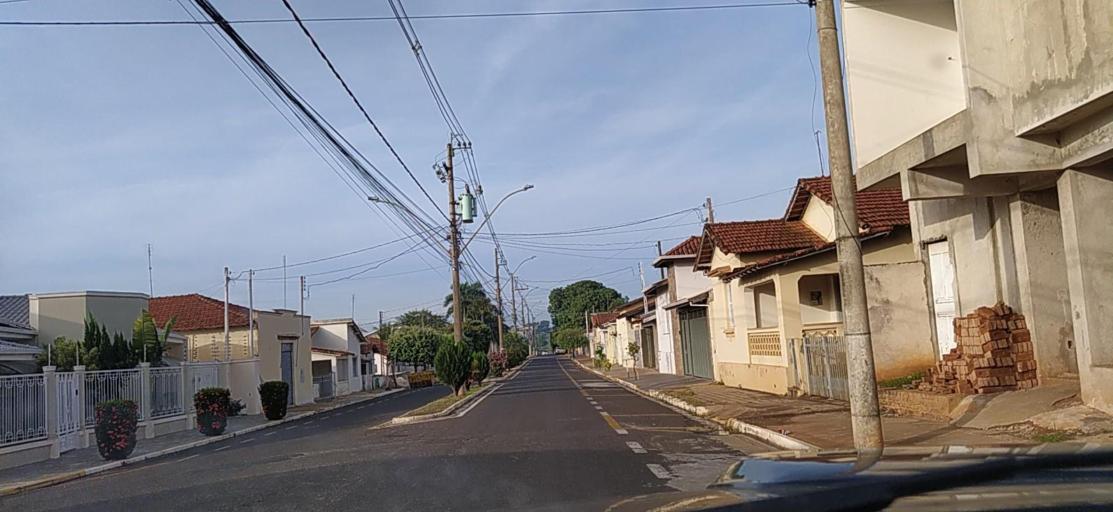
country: BR
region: Sao Paulo
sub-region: Pindorama
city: Pindorama
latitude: -21.1896
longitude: -48.9103
